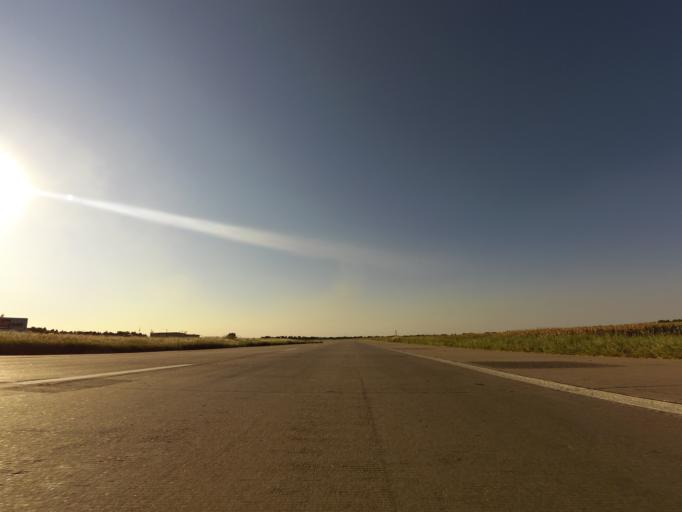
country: US
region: Kansas
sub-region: Sedgwick County
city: Colwich
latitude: 37.8712
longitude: -97.6256
